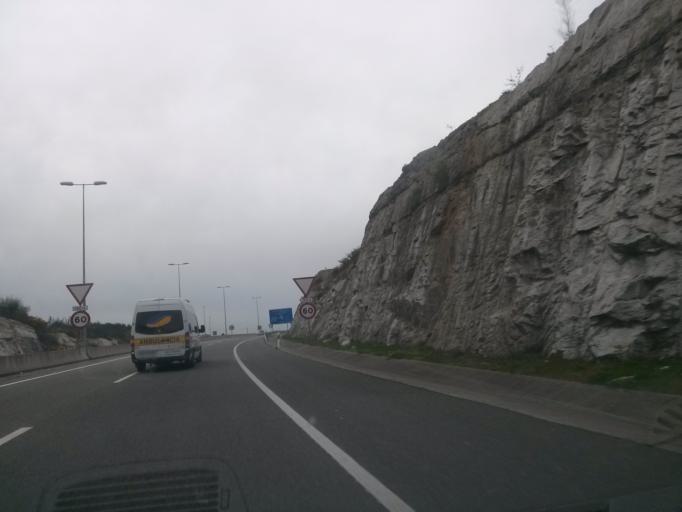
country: ES
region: Galicia
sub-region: Provincia de Lugo
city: Lugo
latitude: 43.0226
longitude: -7.5273
